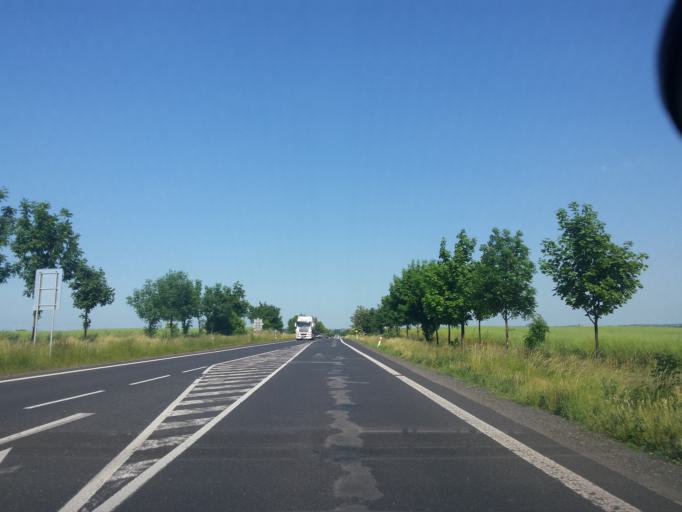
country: CZ
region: Central Bohemia
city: Luzec nad Vltavou
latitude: 50.3400
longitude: 14.3884
